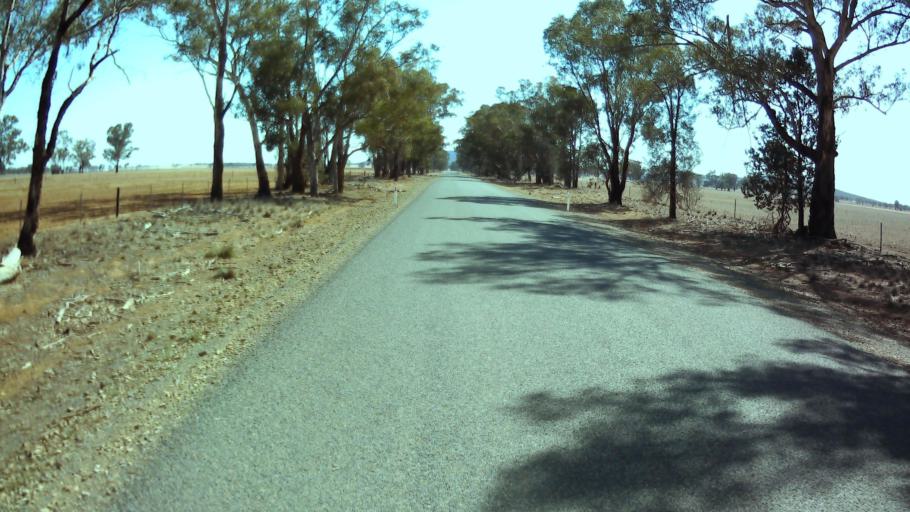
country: AU
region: New South Wales
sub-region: Weddin
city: Grenfell
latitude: -33.7184
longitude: 147.9026
